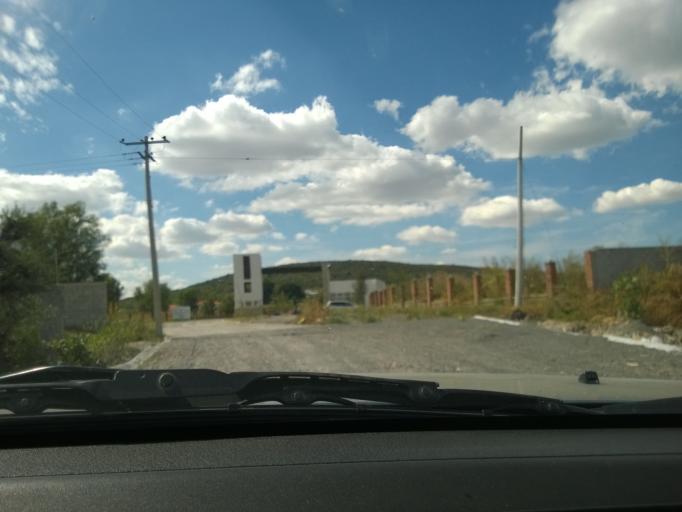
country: MX
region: Guanajuato
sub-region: Leon
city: Plan Guanajuato (La Sandia)
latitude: 20.9456
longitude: -101.7340
